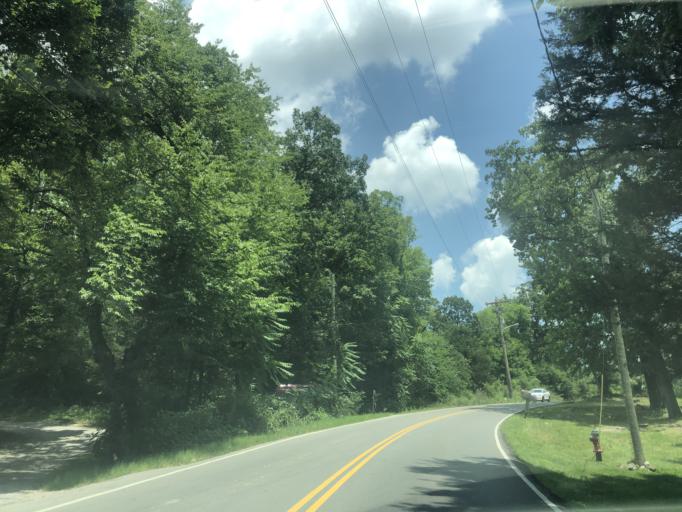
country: US
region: Tennessee
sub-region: Rutherford County
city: La Vergne
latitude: 36.0547
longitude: -86.6528
